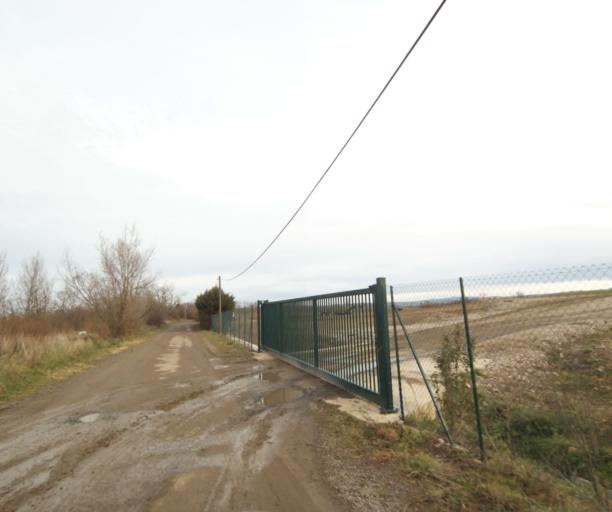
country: FR
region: Rhone-Alpes
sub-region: Departement de la Loire
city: Sury-le-Comtal
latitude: 45.5231
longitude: 4.1907
